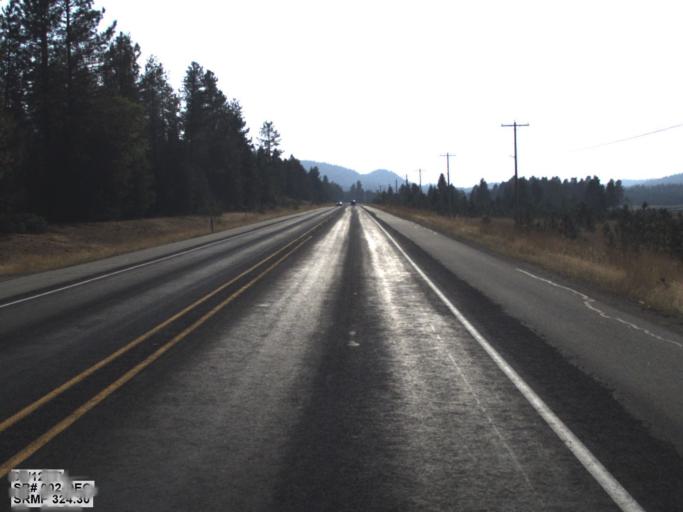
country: US
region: Washington
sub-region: Pend Oreille County
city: Newport
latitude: 48.1124
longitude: -117.2218
